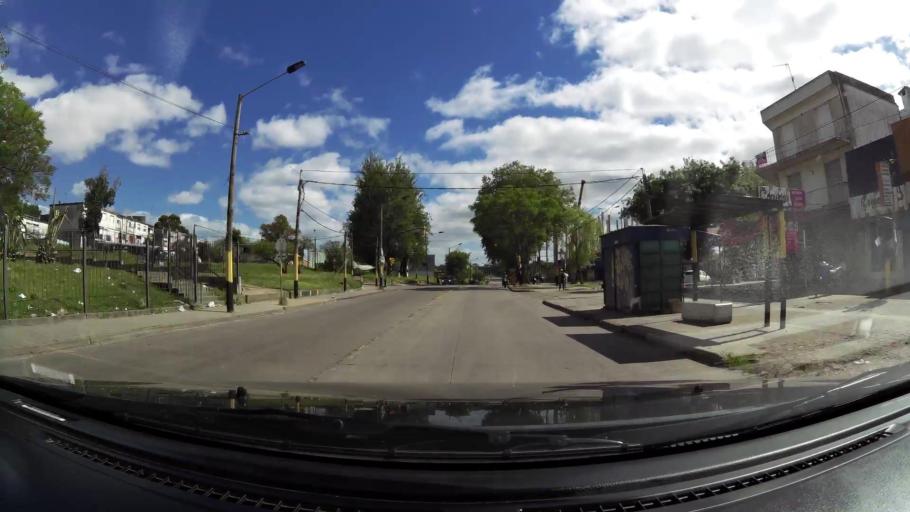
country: UY
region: Canelones
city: Paso de Carrasco
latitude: -34.8813
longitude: -56.1115
